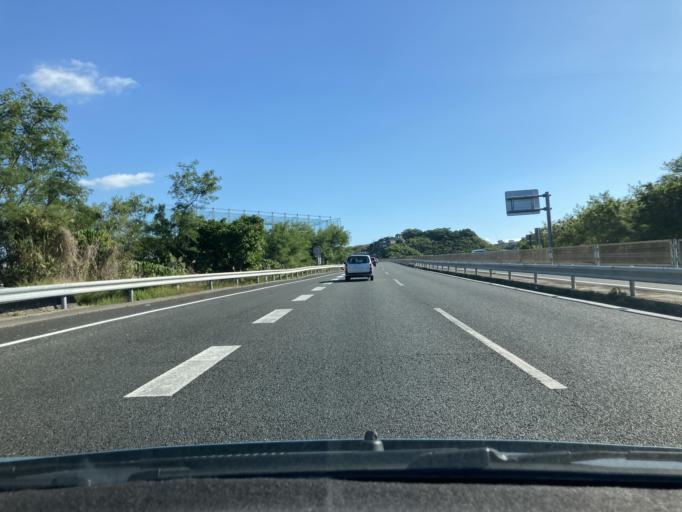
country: JP
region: Okinawa
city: Ginowan
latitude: 26.2483
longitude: 127.7533
